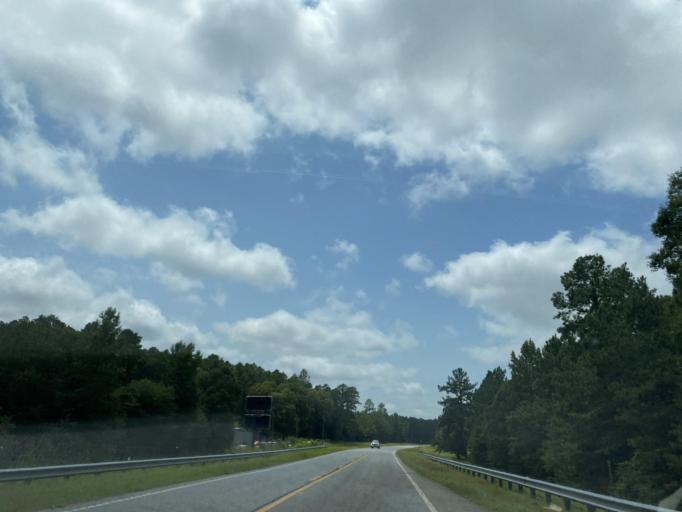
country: US
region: Georgia
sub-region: Wheeler County
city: Alamo
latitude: 32.1283
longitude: -82.7866
